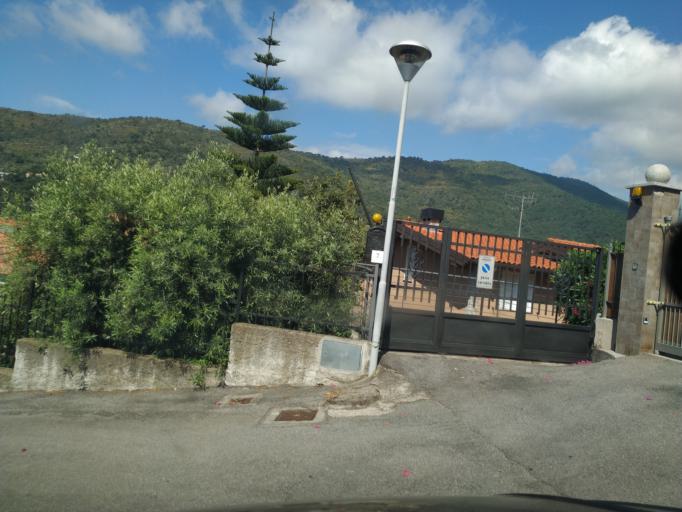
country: IT
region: Liguria
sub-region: Provincia di Savona
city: Andora
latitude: 43.9590
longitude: 8.1467
